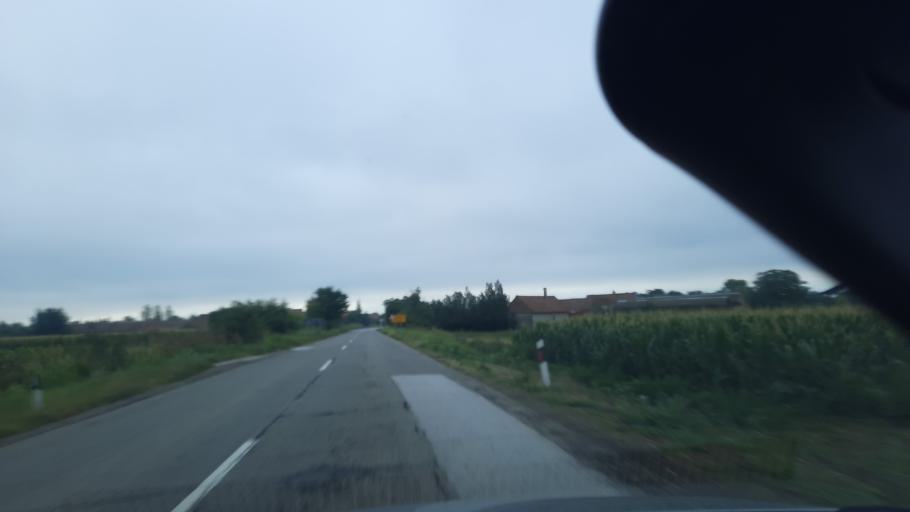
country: RS
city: Farkazdin
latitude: 45.1917
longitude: 20.4648
